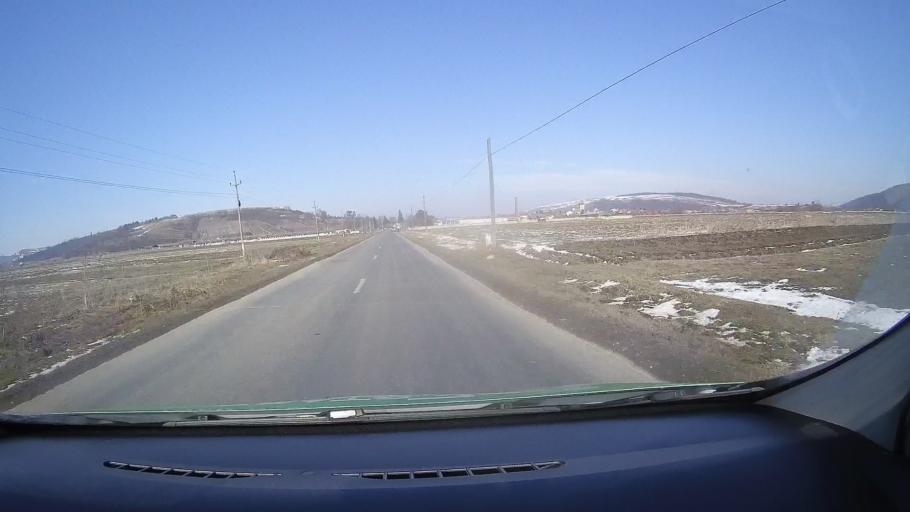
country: RO
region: Brasov
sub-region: Comuna Homorod
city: Homorod
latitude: 46.0312
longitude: 25.2737
